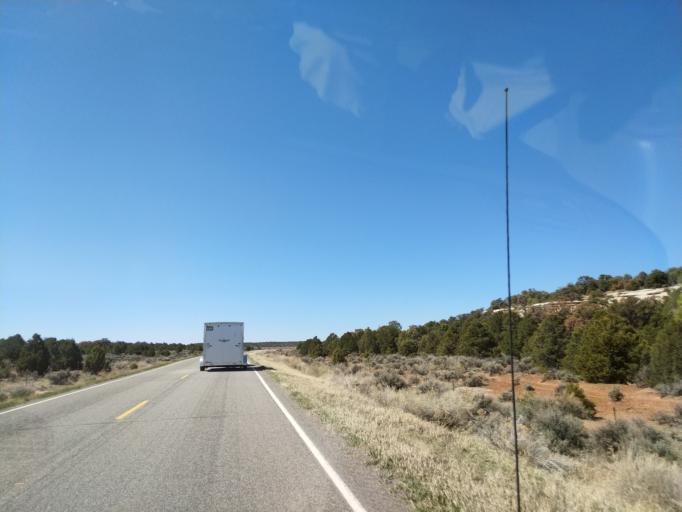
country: US
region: Colorado
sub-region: Mesa County
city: Redlands
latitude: 39.0069
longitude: -108.6865
